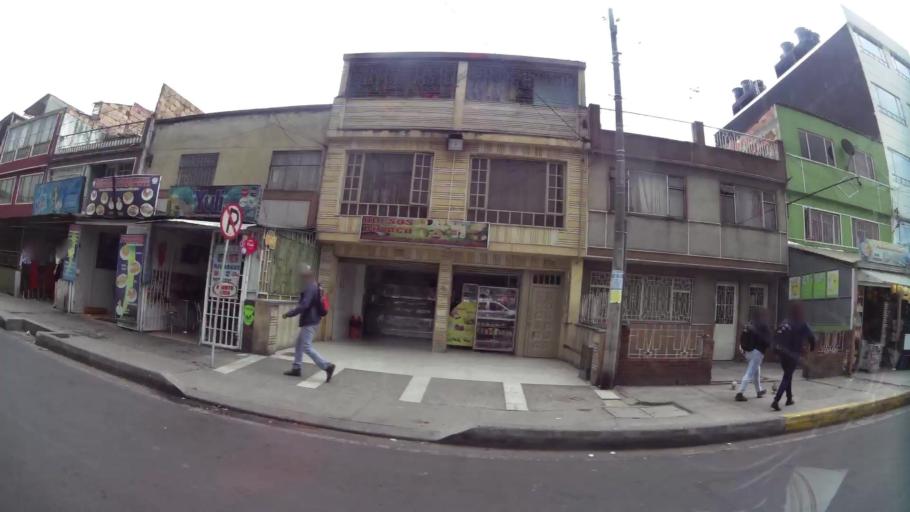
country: CO
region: Bogota D.C.
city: Bogota
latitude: 4.6143
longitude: -74.1111
